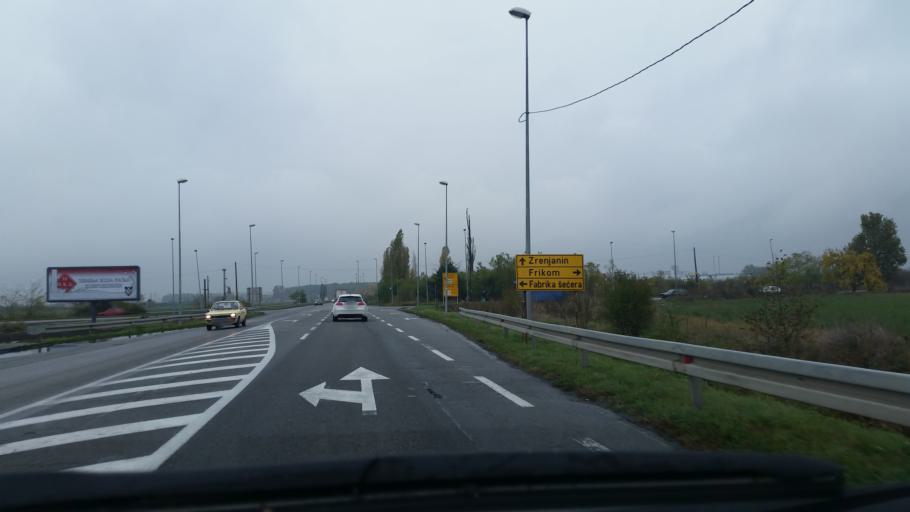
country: RS
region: Central Serbia
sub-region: Belgrade
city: Zemun
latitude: 44.9156
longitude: 20.4420
